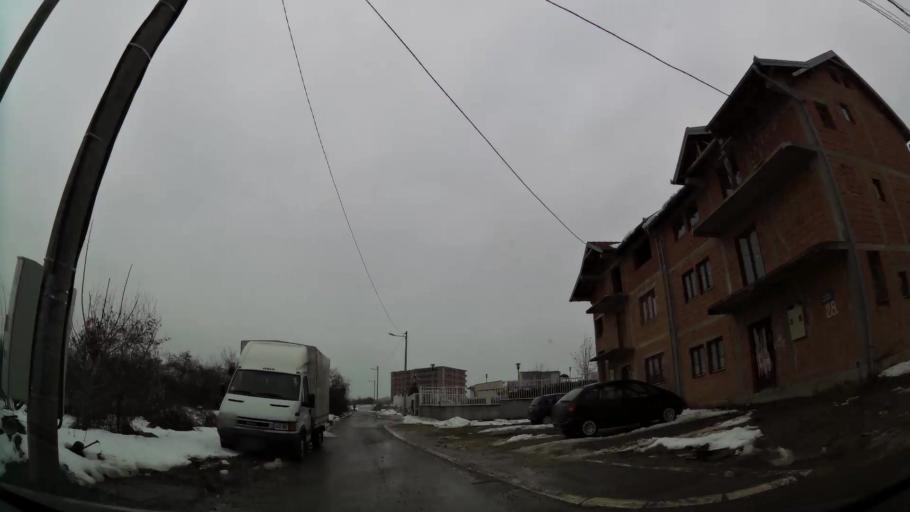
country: RS
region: Central Serbia
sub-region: Belgrade
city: Zvezdara
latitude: 44.7658
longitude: 20.5101
